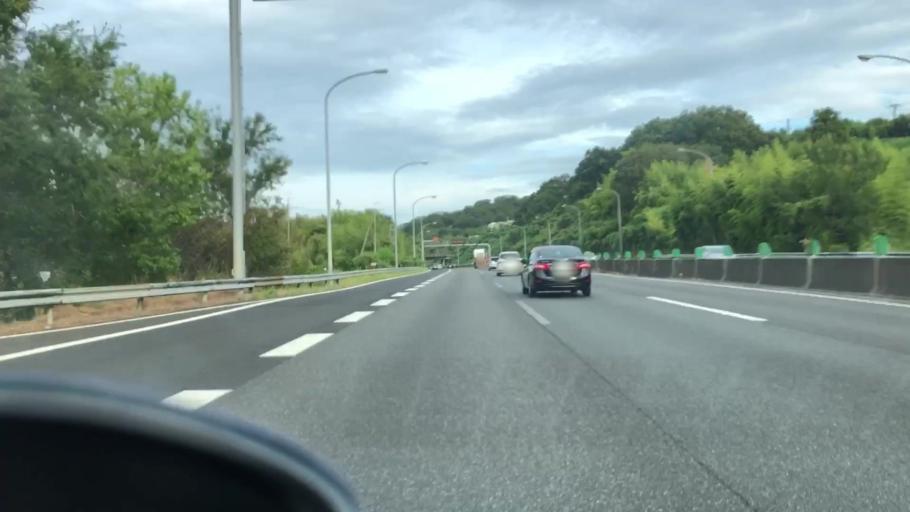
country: JP
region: Hyogo
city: Sandacho
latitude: 34.8379
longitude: 135.2484
